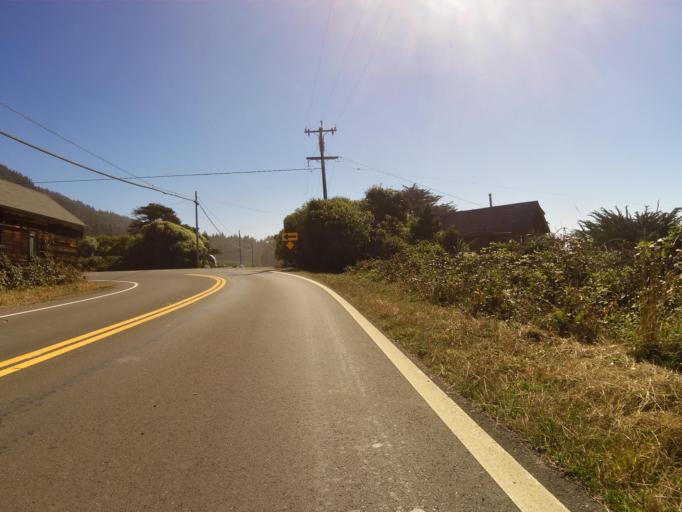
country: US
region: California
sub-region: Mendocino County
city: Fort Bragg
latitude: 39.6362
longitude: -123.7849
